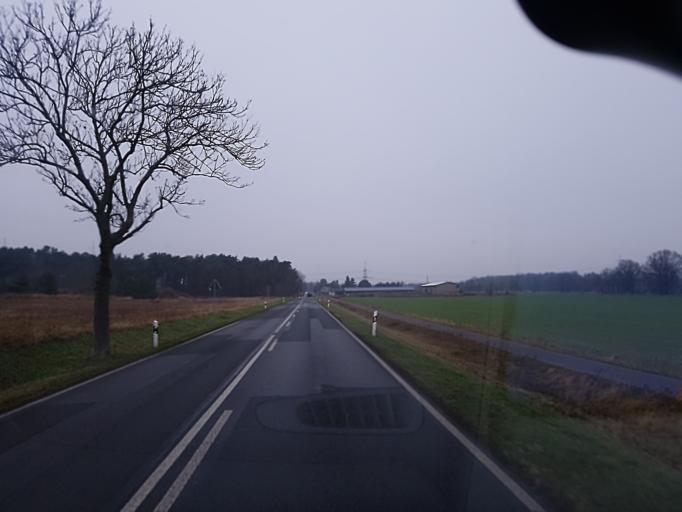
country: DE
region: Brandenburg
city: Lubbenau
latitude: 51.8777
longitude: 13.9096
